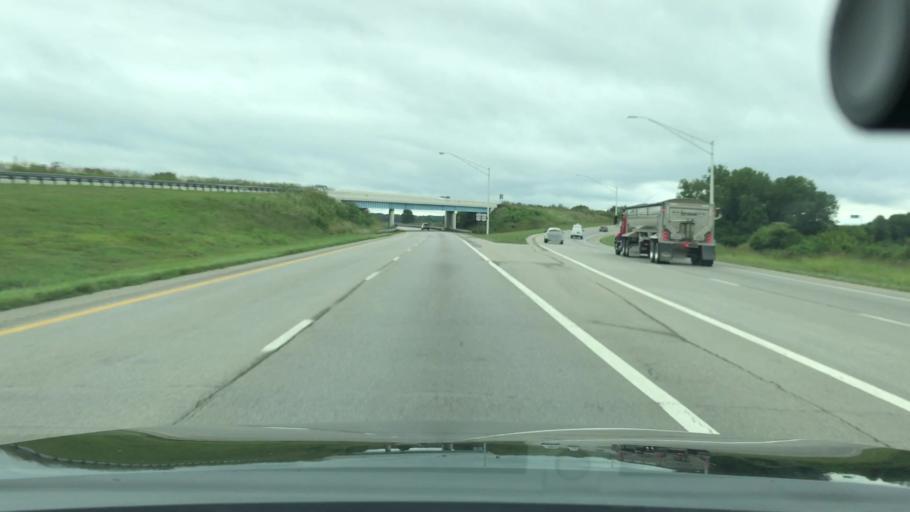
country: US
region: Ohio
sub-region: Ross County
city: Chillicothe
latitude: 39.3228
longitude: -82.9413
